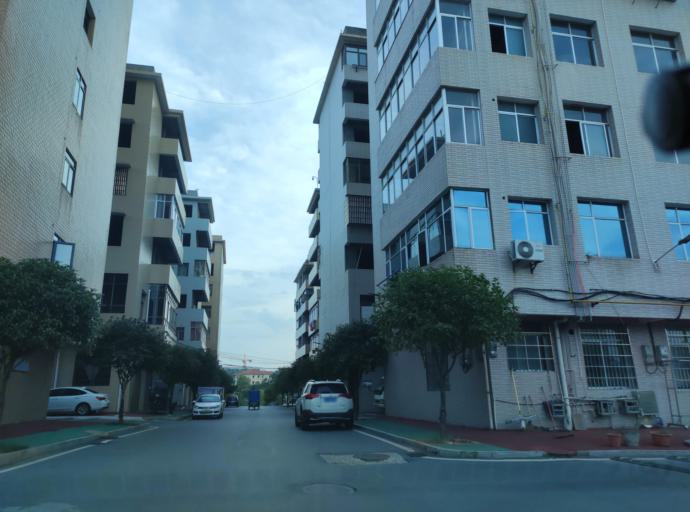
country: CN
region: Jiangxi Sheng
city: Pingxiang
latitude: 27.6405
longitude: 113.8787
